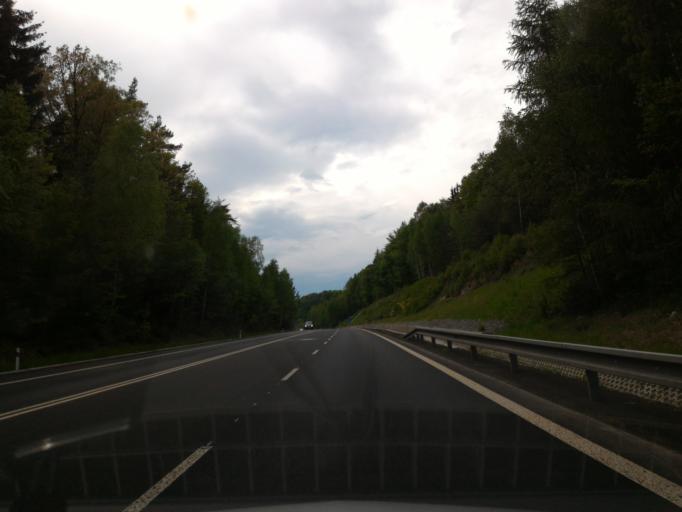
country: CZ
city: Novy Bor
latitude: 50.7734
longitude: 14.5557
